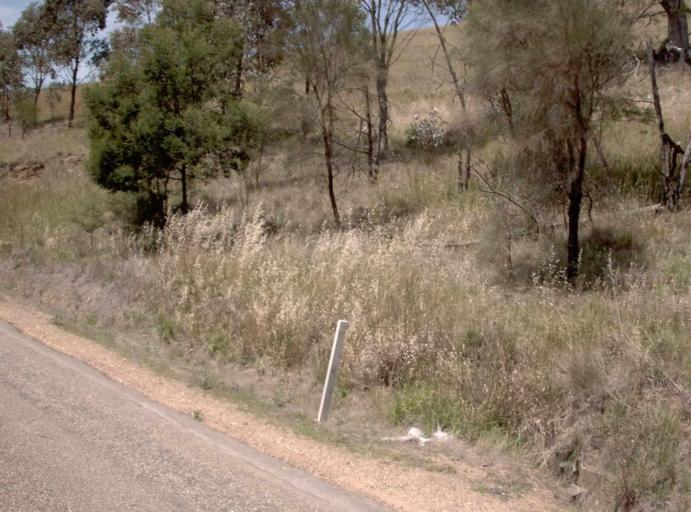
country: AU
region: Victoria
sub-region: East Gippsland
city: Bairnsdale
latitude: -37.3596
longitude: 147.8176
